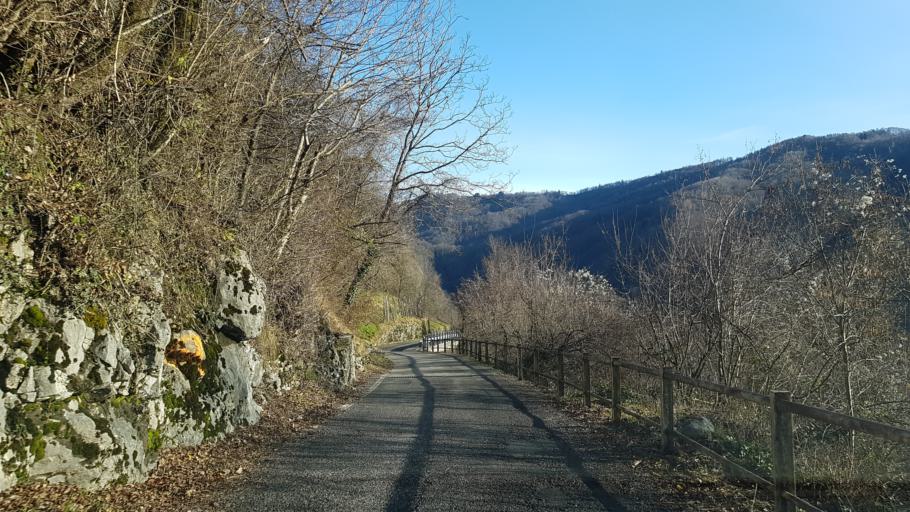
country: IT
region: Friuli Venezia Giulia
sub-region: Provincia di Udine
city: Clodig
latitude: 46.1596
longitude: 13.5853
